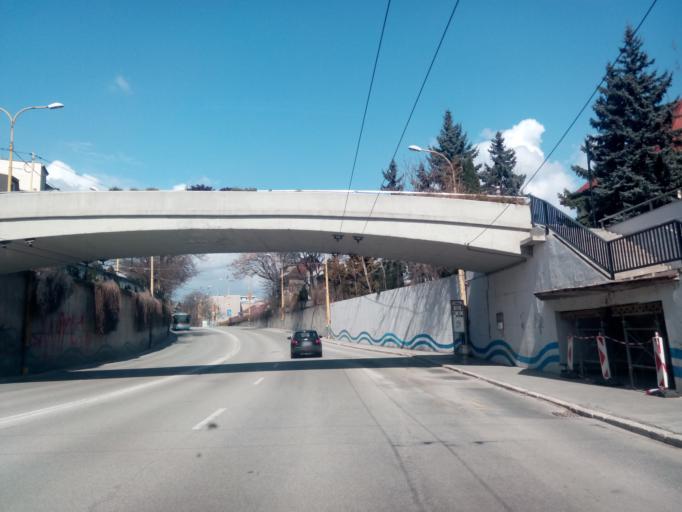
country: SK
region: Kosicky
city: Kosice
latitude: 48.7248
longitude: 21.2605
